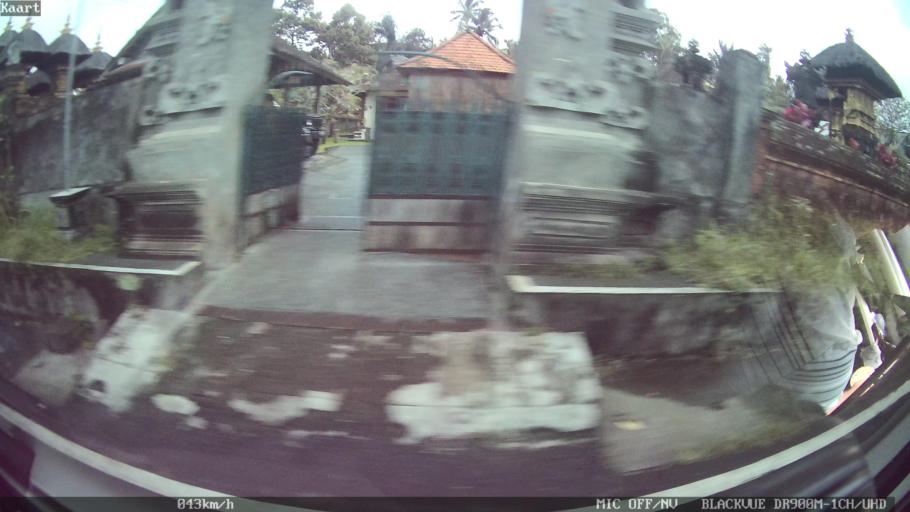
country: ID
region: Bali
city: Pemijian
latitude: -8.4491
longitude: 115.2284
